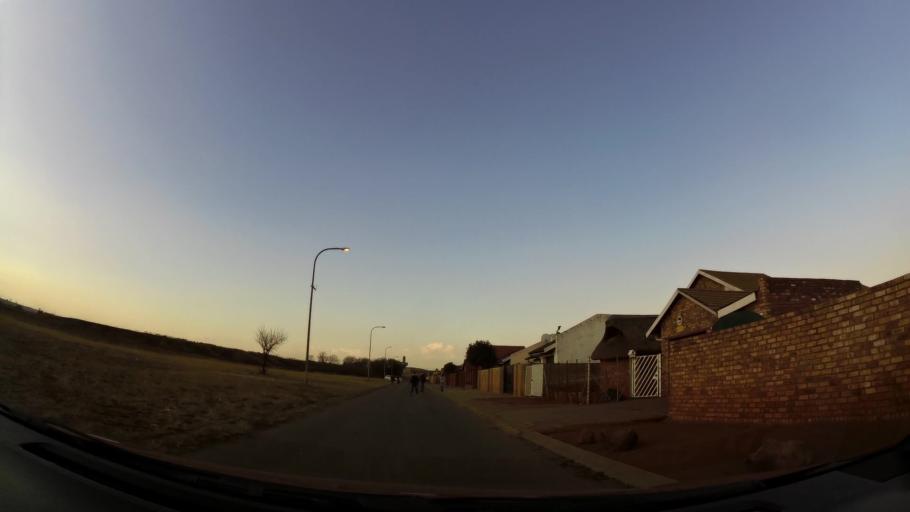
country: ZA
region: Gauteng
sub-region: City of Johannesburg Metropolitan Municipality
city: Soweto
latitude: -26.2204
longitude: 27.8539
